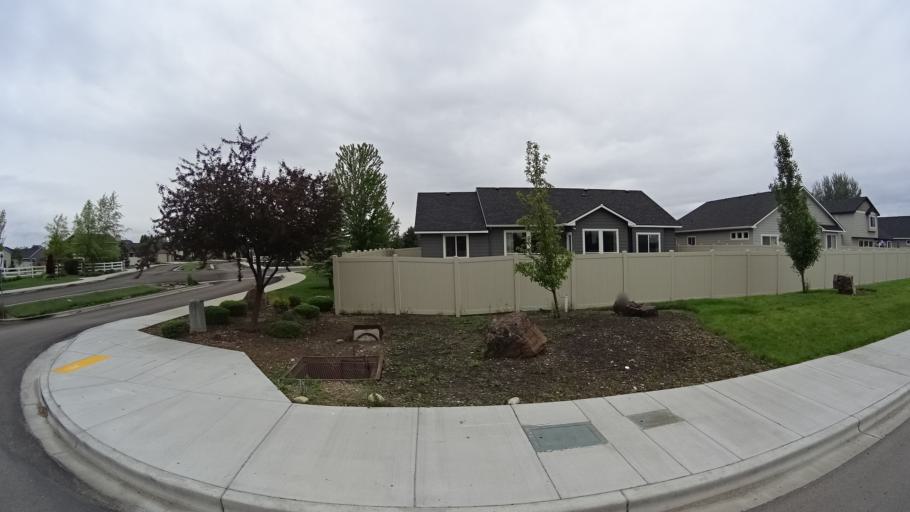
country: US
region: Idaho
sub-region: Ada County
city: Meridian
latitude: 43.6336
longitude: -116.4103
